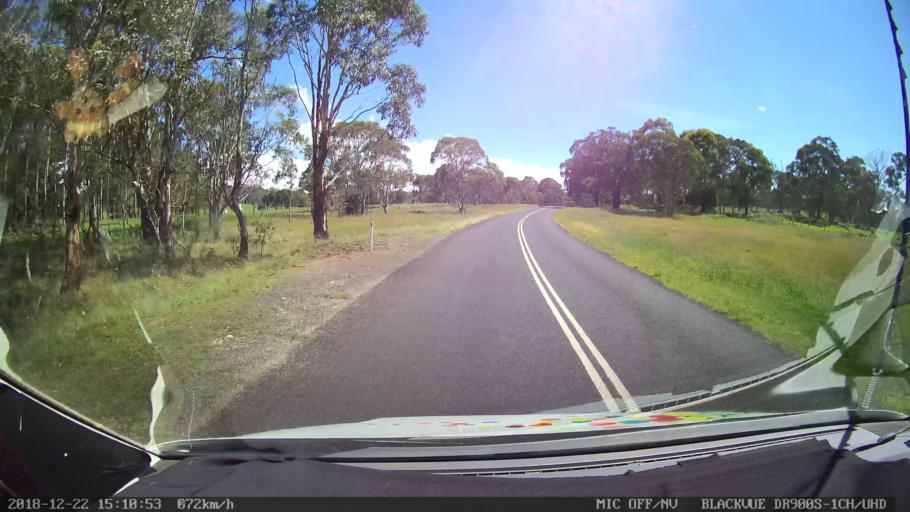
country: AU
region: New South Wales
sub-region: Bellingen
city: Dorrigo
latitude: -30.3397
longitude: 152.4066
